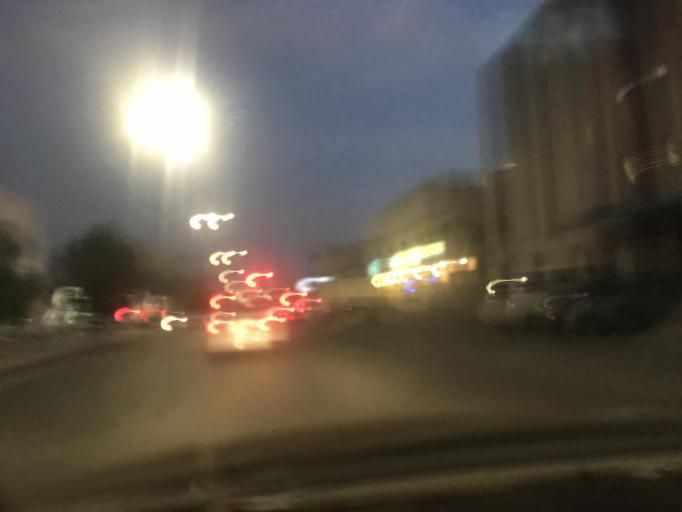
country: SA
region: Ar Riyad
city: Riyadh
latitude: 24.7320
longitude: 46.7614
